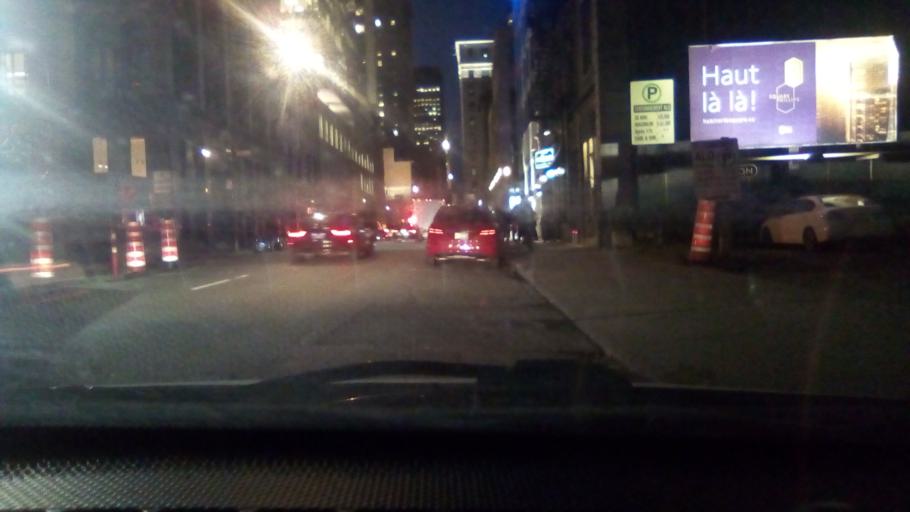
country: CA
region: Quebec
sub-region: Montreal
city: Montreal
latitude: 45.4996
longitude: -73.5603
